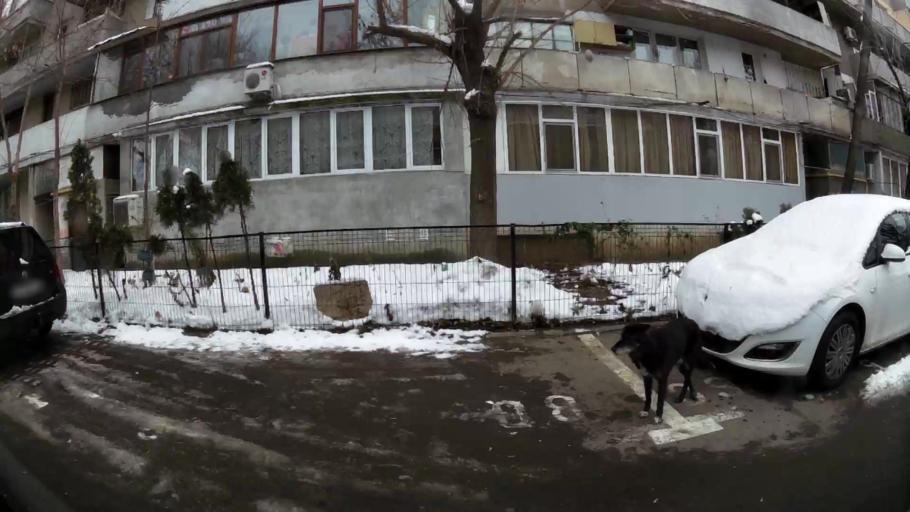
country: RO
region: Bucuresti
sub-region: Municipiul Bucuresti
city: Bucuresti
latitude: 44.3927
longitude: 26.1175
